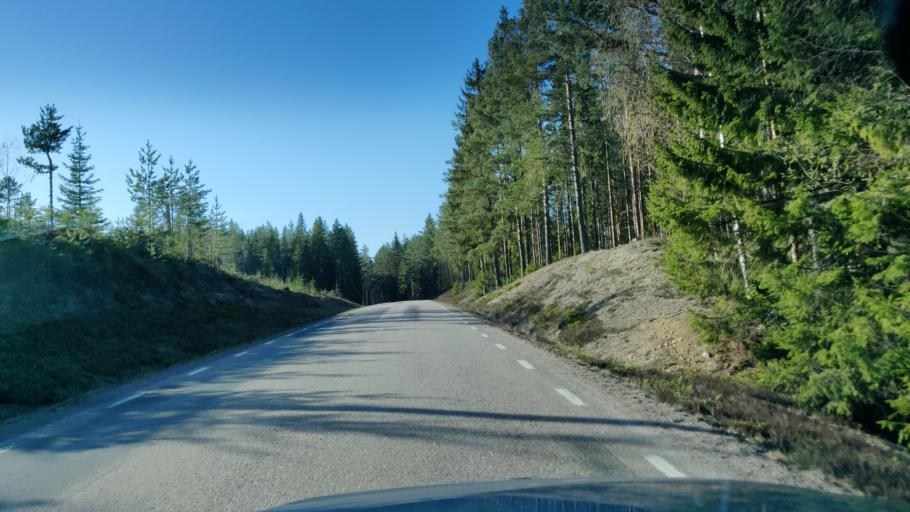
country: SE
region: Vaermland
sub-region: Sunne Kommun
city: Sunne
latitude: 59.9903
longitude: 13.3100
